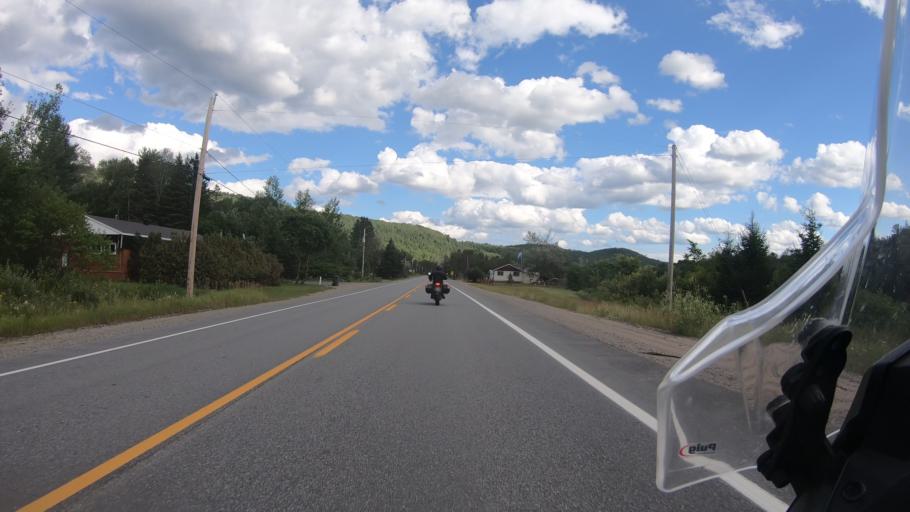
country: CA
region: Quebec
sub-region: Mauricie
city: Saint-Tite
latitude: 46.9846
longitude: -72.9093
